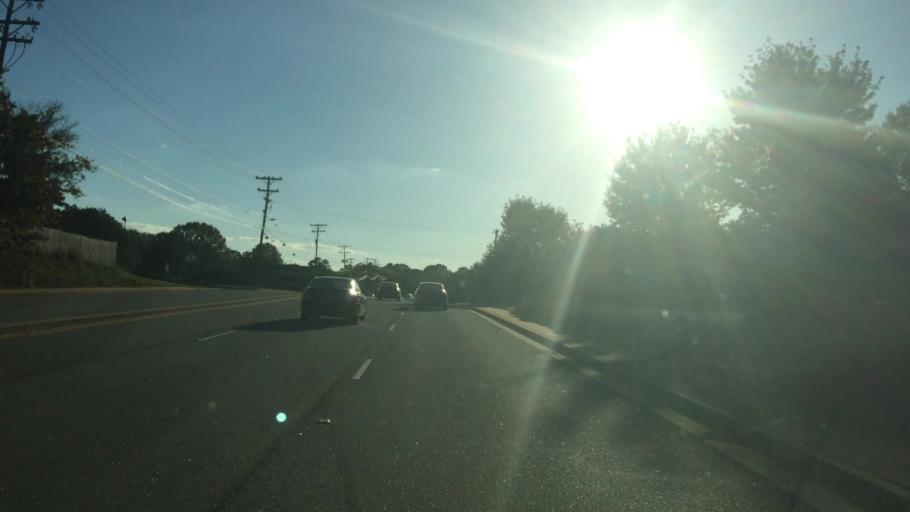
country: US
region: South Carolina
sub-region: Greenville County
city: Wade Hampton
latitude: 34.8585
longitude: -82.2977
